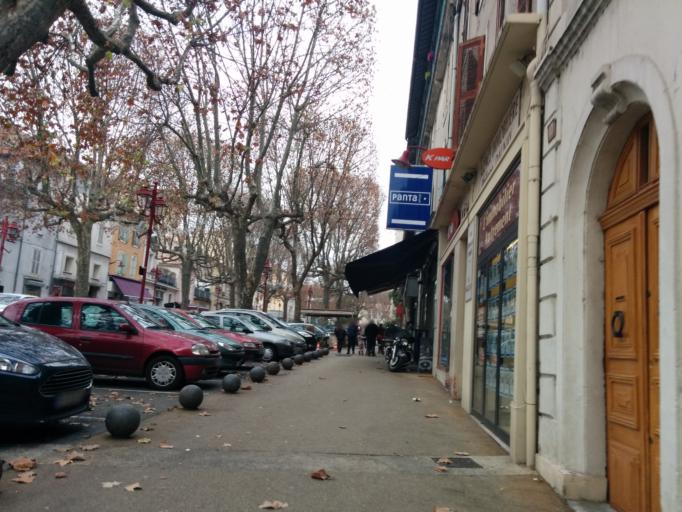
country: FR
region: Languedoc-Roussillon
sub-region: Departement du Gard
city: Ales
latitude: 44.1249
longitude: 4.0803
